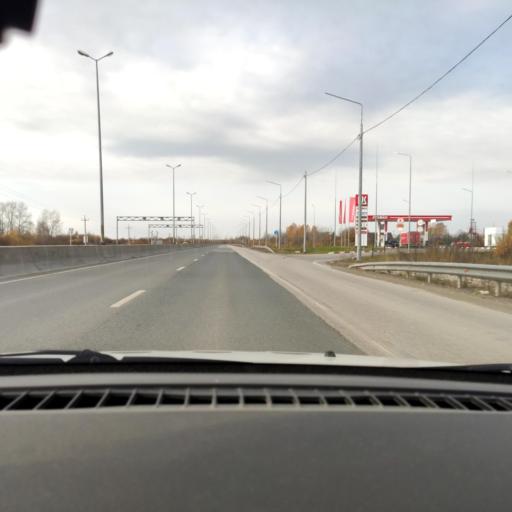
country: RU
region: Perm
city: Kondratovo
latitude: 58.0004
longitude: 56.1063
